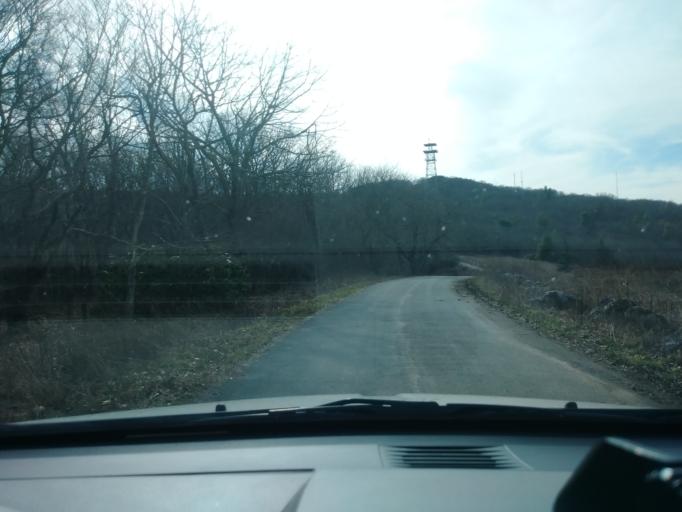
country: US
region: Tennessee
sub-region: Greene County
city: Tusculum
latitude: 36.0297
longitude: -82.7085
